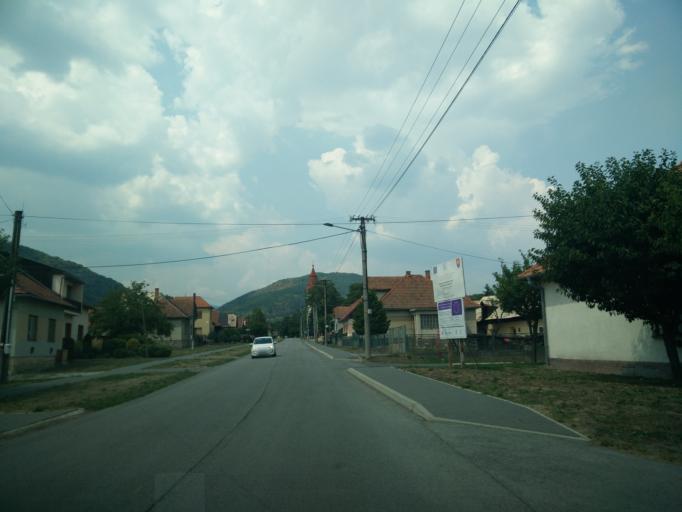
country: SK
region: Banskobystricky
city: Zarnovica
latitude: 48.5672
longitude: 18.7513
